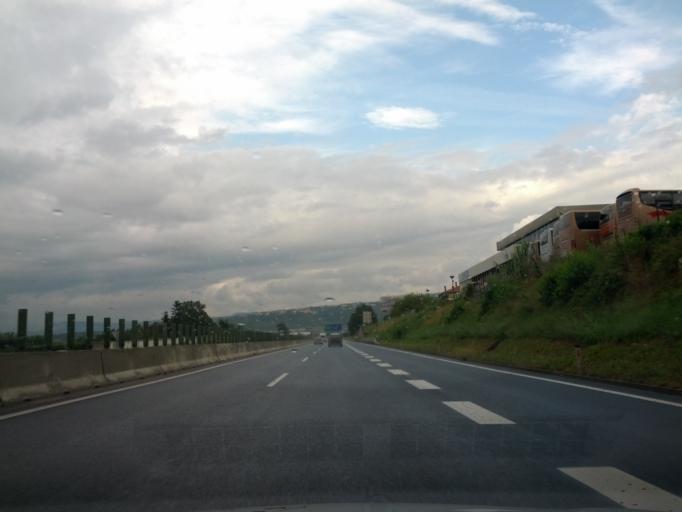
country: SI
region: Koper-Capodistria
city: Prade
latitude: 45.5468
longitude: 13.7638
